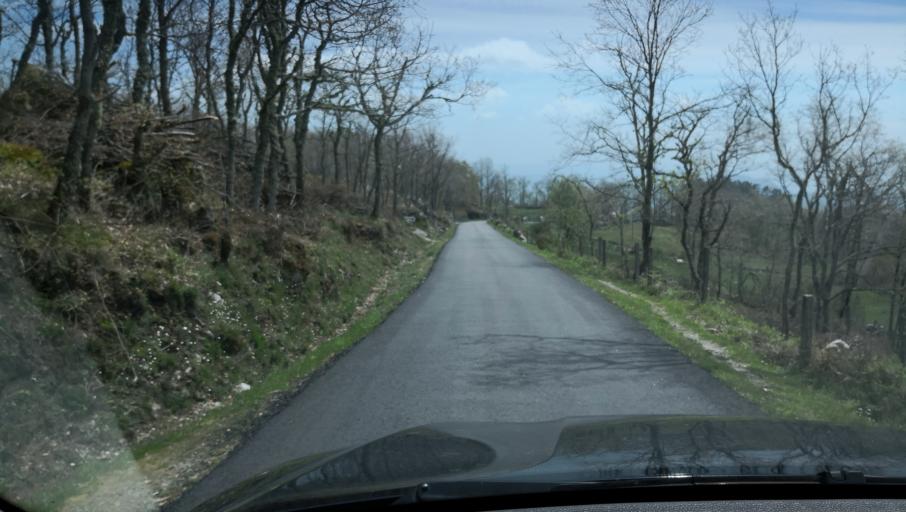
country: PT
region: Vila Real
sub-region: Vila Real
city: Vila Real
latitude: 41.2939
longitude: -7.8215
